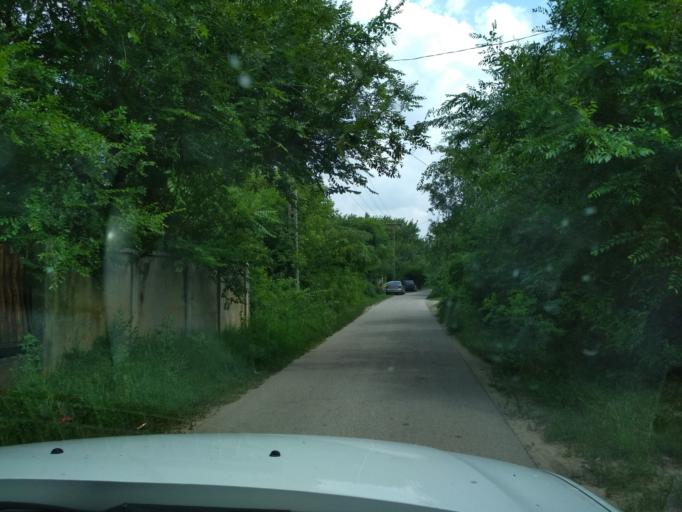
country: HU
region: Pest
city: Tapioszentmarton
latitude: 47.3708
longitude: 19.7589
